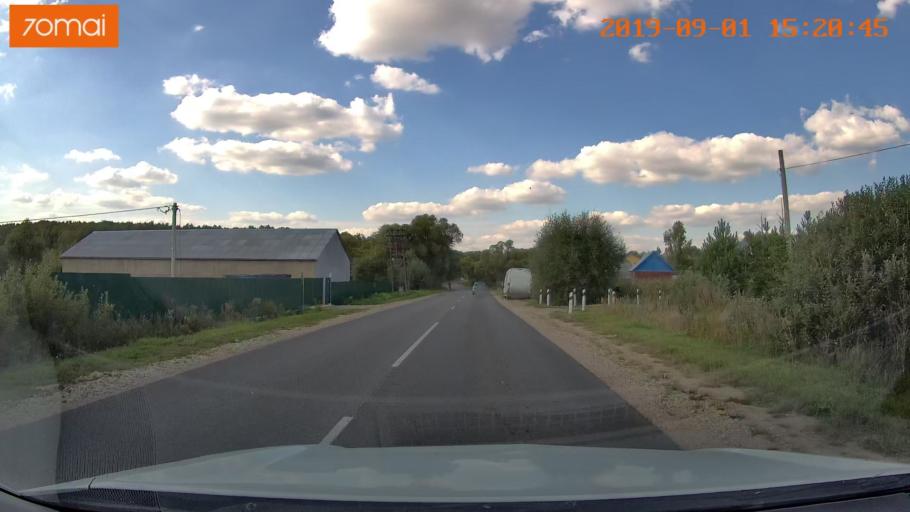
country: RU
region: Kaluga
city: Maloyaroslavets
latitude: 54.9225
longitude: 36.4773
